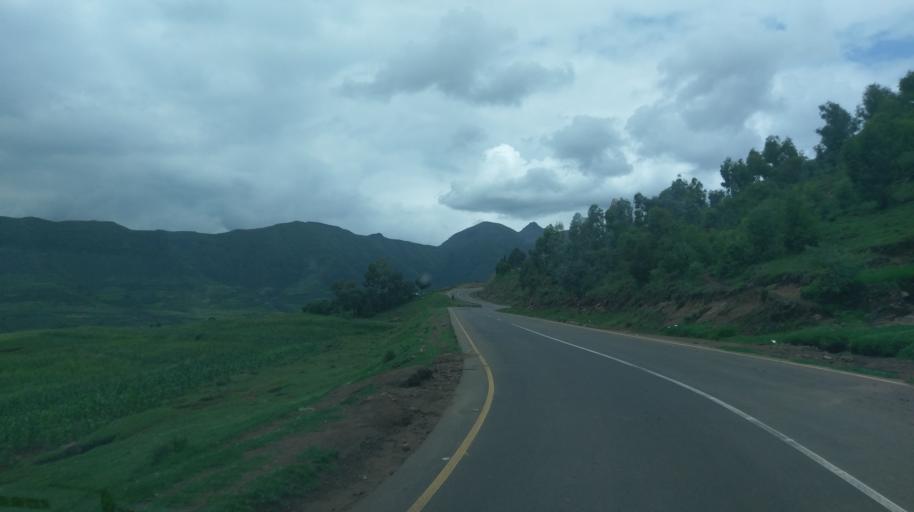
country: LS
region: Butha-Buthe
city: Butha-Buthe
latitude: -29.0361
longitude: 28.2879
